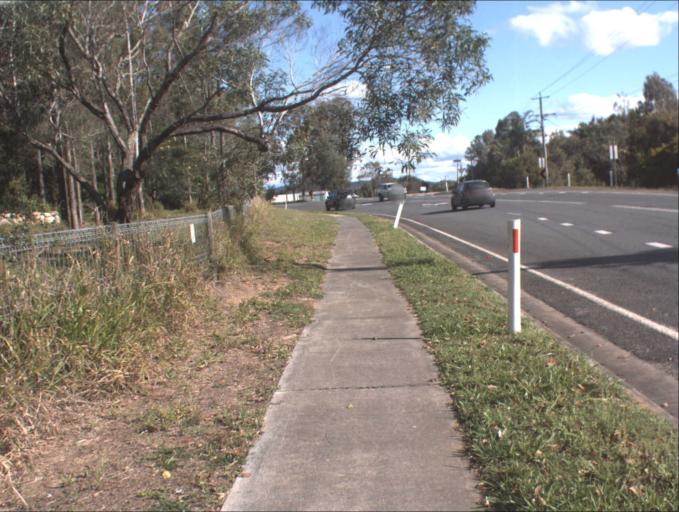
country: AU
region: Queensland
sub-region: Logan
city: Chambers Flat
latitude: -27.7597
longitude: 153.0912
